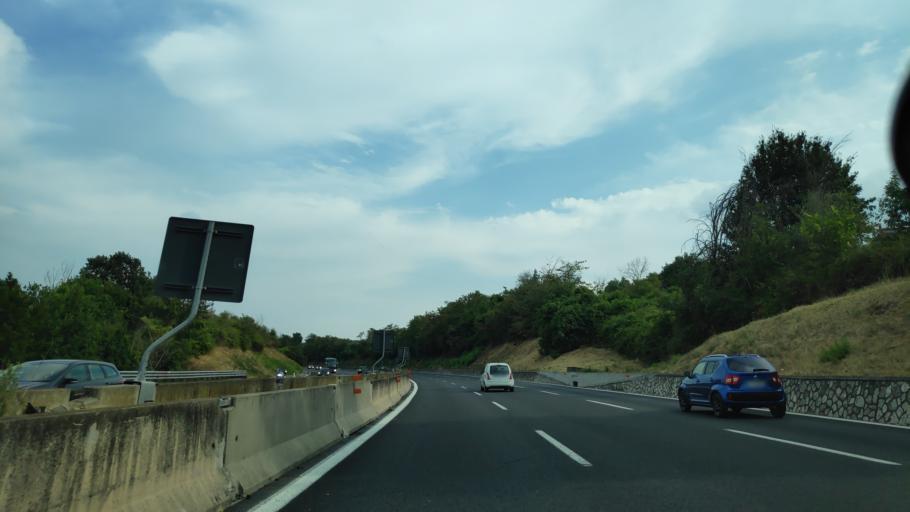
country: IT
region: Latium
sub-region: Citta metropolitana di Roma Capitale
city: Fiano Romano
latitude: 42.1806
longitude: 12.6023
